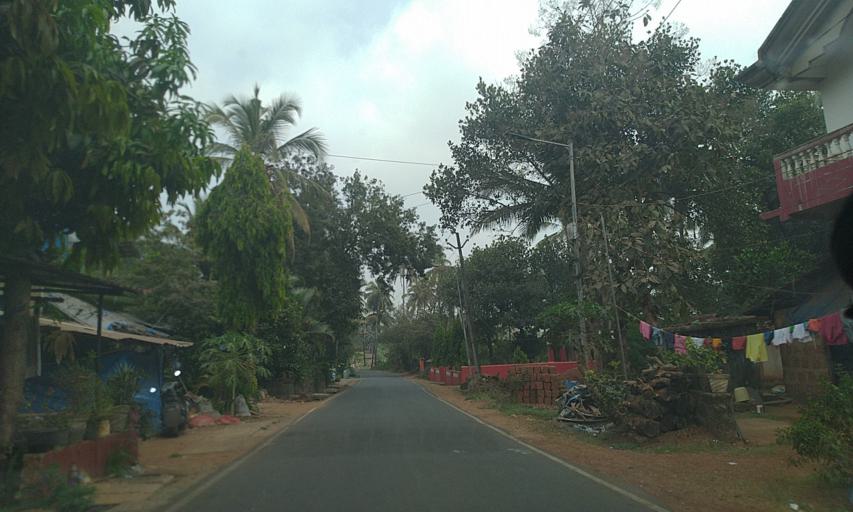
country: IN
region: Goa
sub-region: South Goa
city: Raia
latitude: 15.3080
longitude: 73.9570
